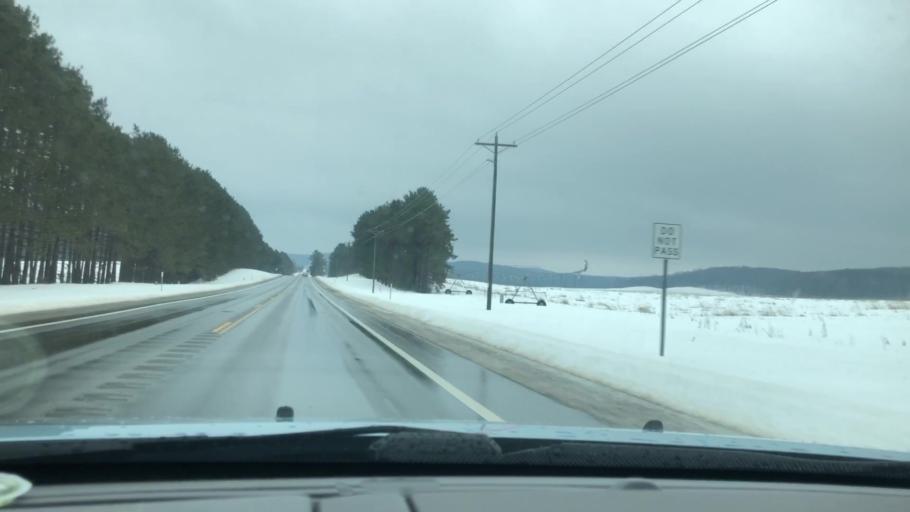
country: US
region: Michigan
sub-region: Charlevoix County
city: Boyne City
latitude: 45.0945
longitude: -84.9704
